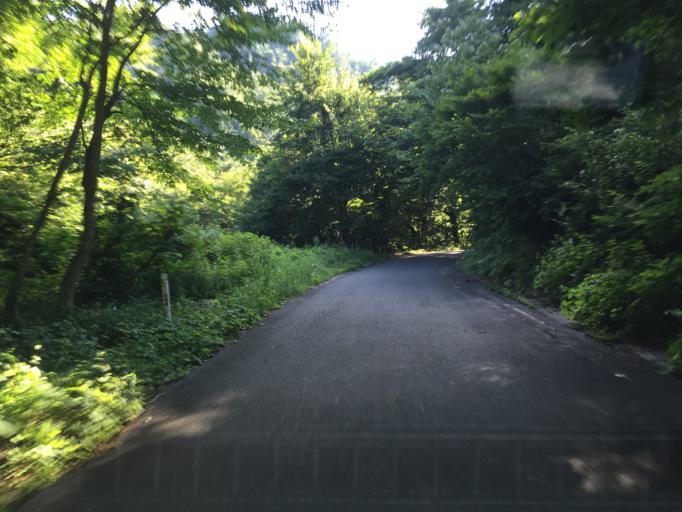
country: JP
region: Yamagata
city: Takahata
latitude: 37.9648
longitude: 140.3416
